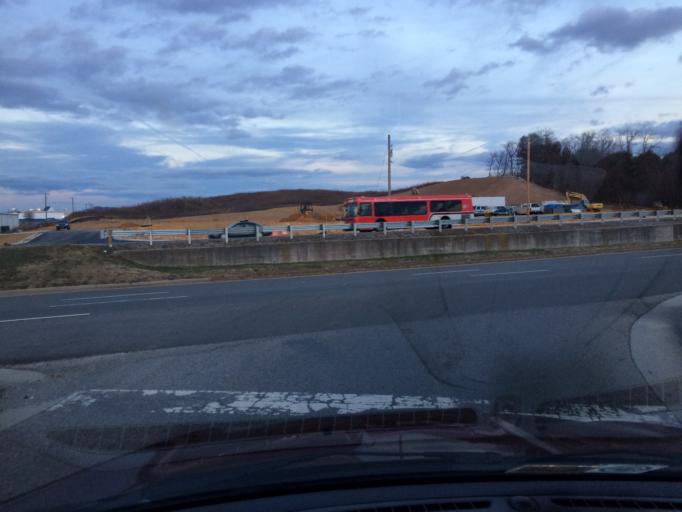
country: US
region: Virginia
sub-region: Montgomery County
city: Merrimac
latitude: 37.1592
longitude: -80.4210
